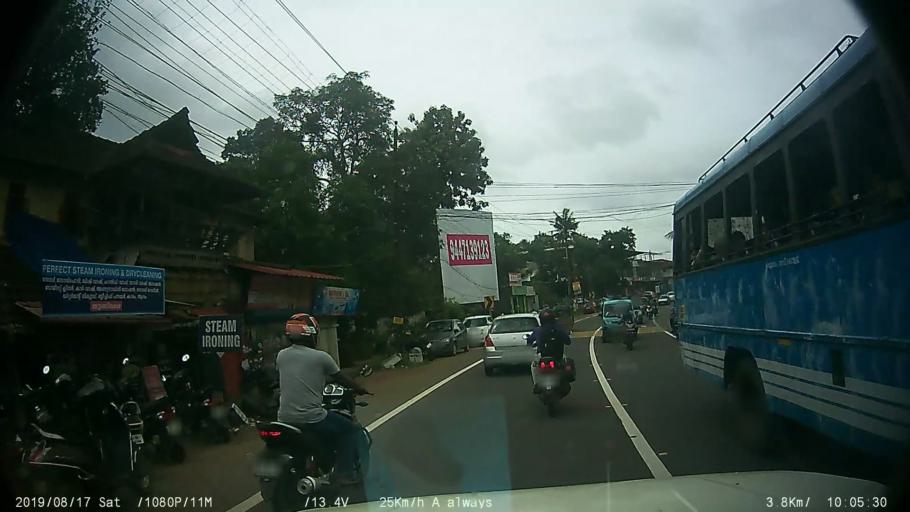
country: IN
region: Kerala
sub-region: Kottayam
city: Kottayam
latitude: 9.6105
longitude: 76.5323
